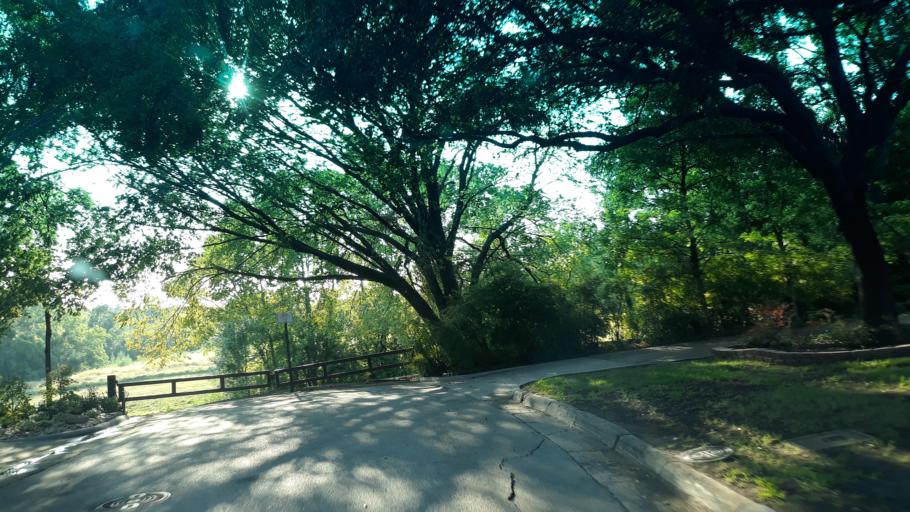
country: US
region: Texas
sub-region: Dallas County
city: Addison
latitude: 32.9439
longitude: -96.7950
